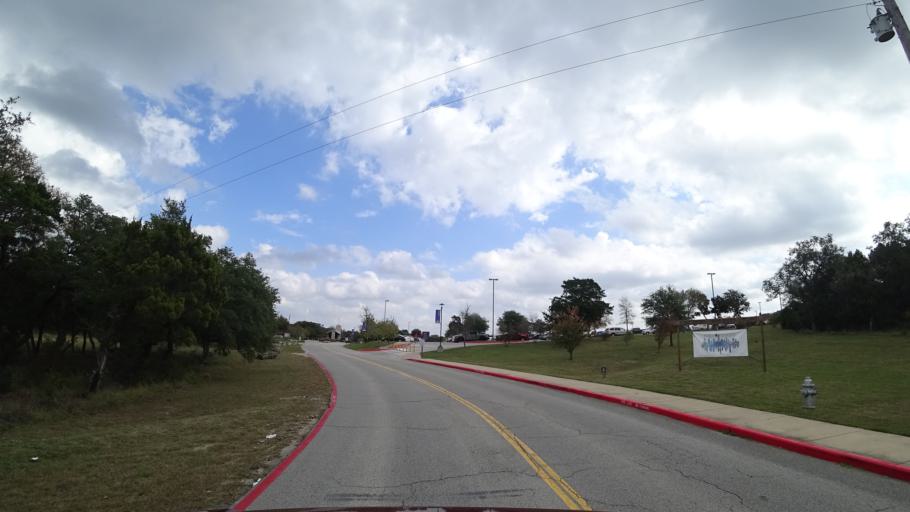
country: US
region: Texas
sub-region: Williamson County
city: Anderson Mill
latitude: 30.4202
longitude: -97.8407
